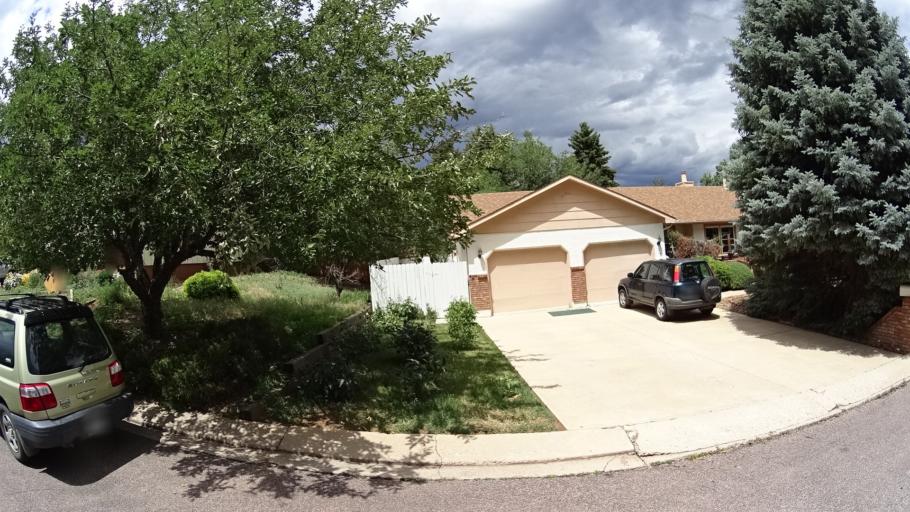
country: US
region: Colorado
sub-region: El Paso County
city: Manitou Springs
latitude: 38.8479
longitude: -104.8929
